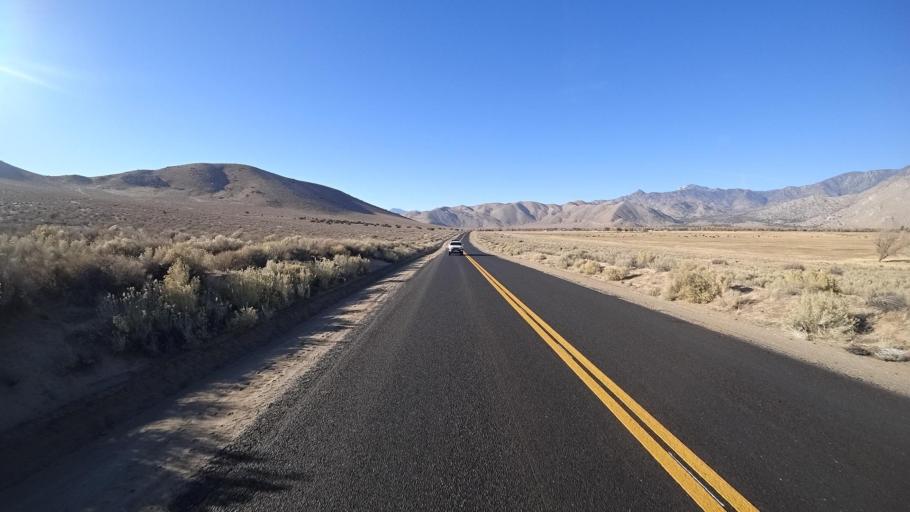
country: US
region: California
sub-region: Kern County
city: Weldon
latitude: 35.6534
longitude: -118.2835
